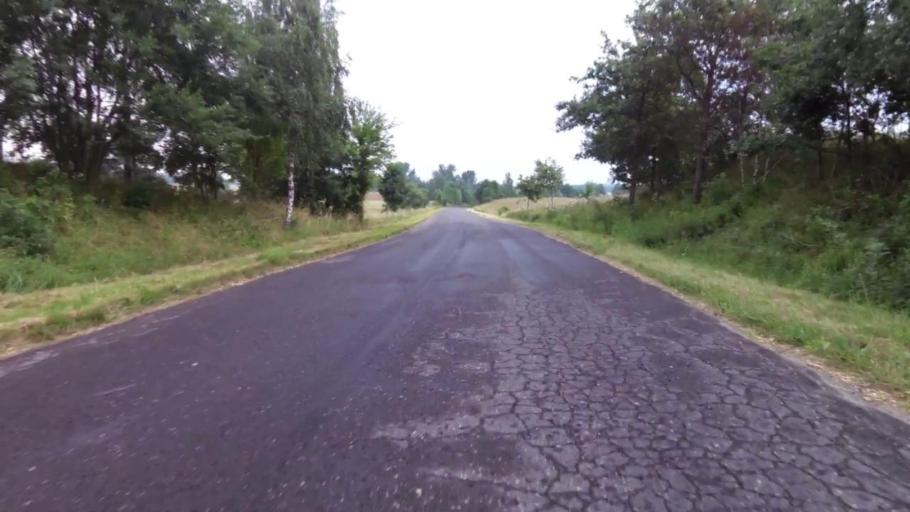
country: PL
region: West Pomeranian Voivodeship
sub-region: Powiat lobeski
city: Wegorzyno
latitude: 53.5029
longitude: 15.6453
